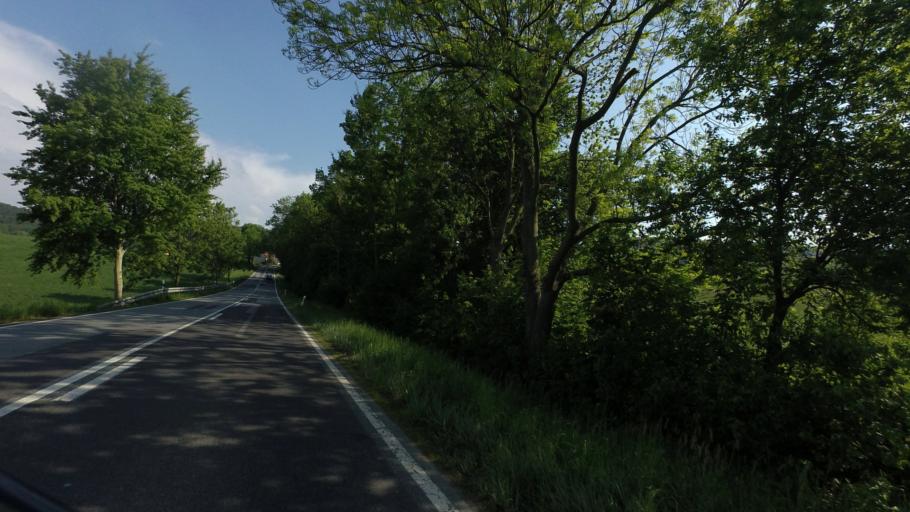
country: DE
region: Saxony
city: Oppach
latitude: 51.0846
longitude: 14.4827
